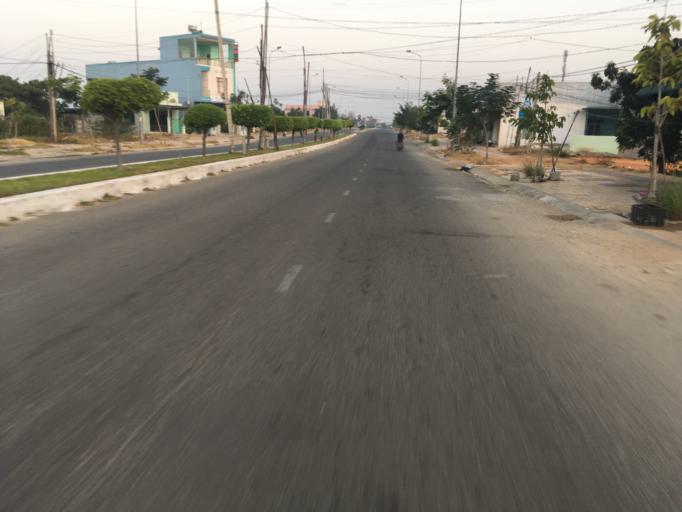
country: VN
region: Ninh Thuan
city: Phan Rang-Thap Cham
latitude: 11.5554
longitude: 109.0233
